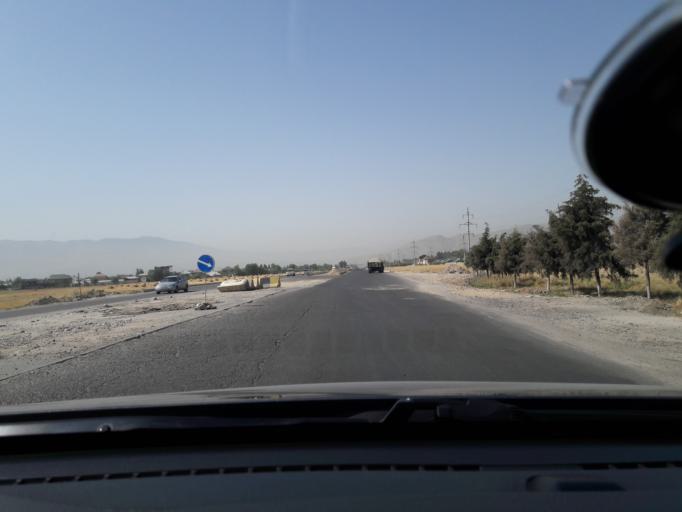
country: TJ
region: Dushanbe
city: Dushanbe
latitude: 38.4975
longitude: 68.7548
